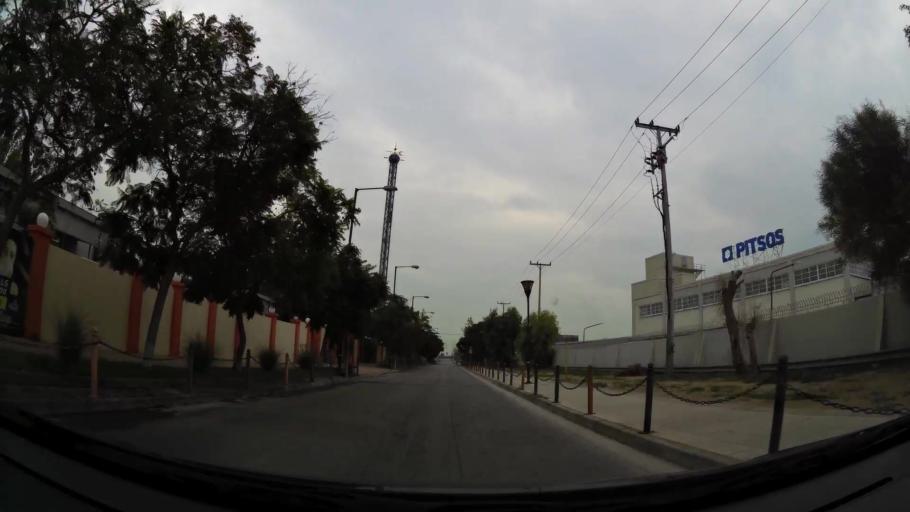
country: GR
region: Attica
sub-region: Nomos Piraios
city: Agios Ioannis Rentis
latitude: 37.9731
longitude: 23.6723
